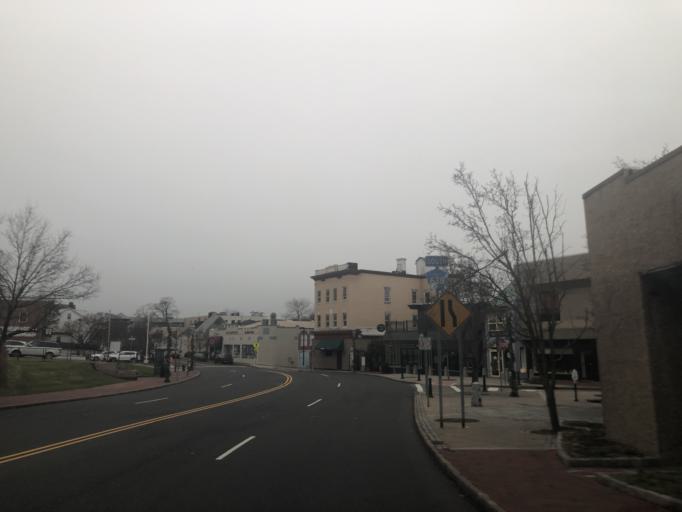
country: US
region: New Jersey
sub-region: Essex County
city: South Orange
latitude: 40.7454
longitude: -74.2585
